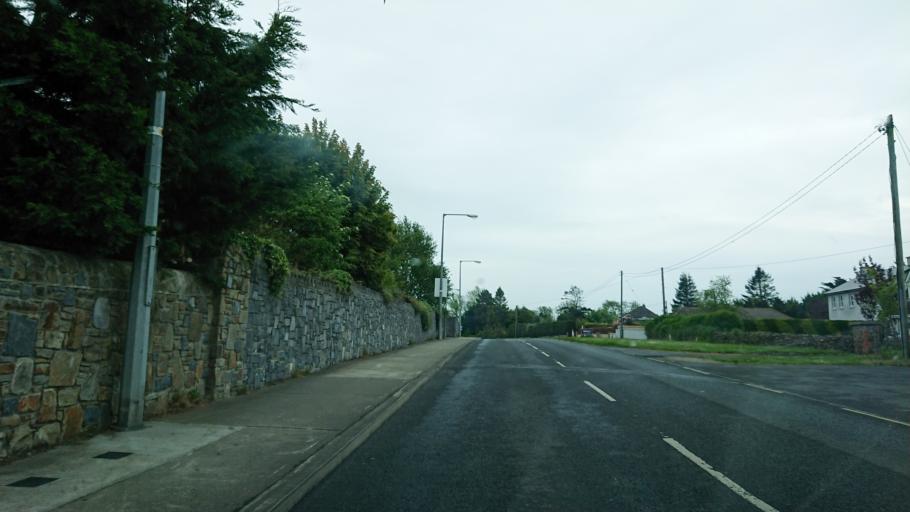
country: IE
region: Munster
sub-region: Waterford
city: Waterford
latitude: 52.2374
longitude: -7.0823
